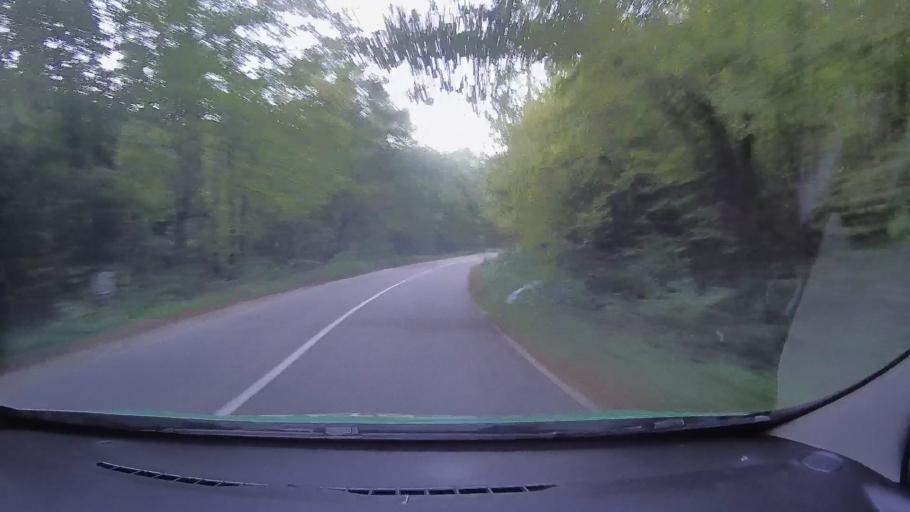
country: RO
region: Timis
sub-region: Comuna Fardea
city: Fardea
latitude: 45.6885
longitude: 22.1572
